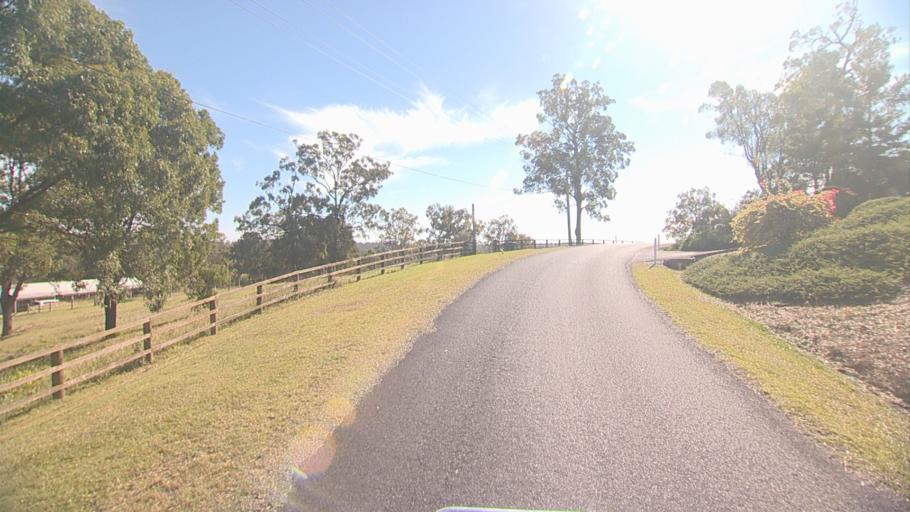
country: AU
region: Queensland
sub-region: Logan
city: Windaroo
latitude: -27.7435
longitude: 153.1720
